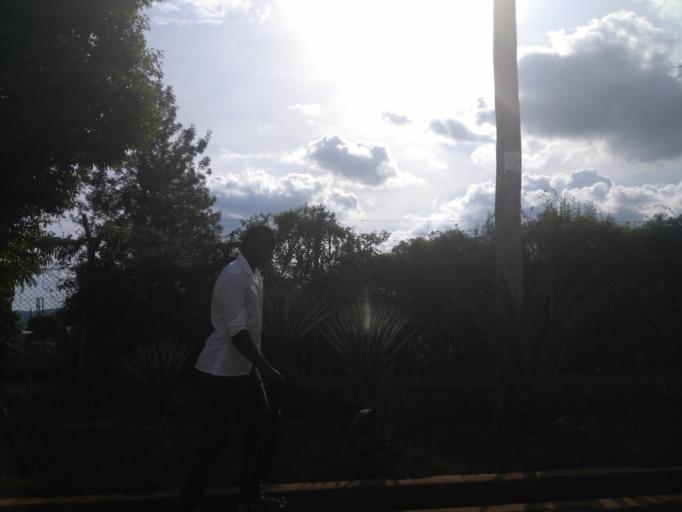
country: UG
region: Eastern Region
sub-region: Jinja District
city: Jinja
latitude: 0.4161
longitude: 33.2147
